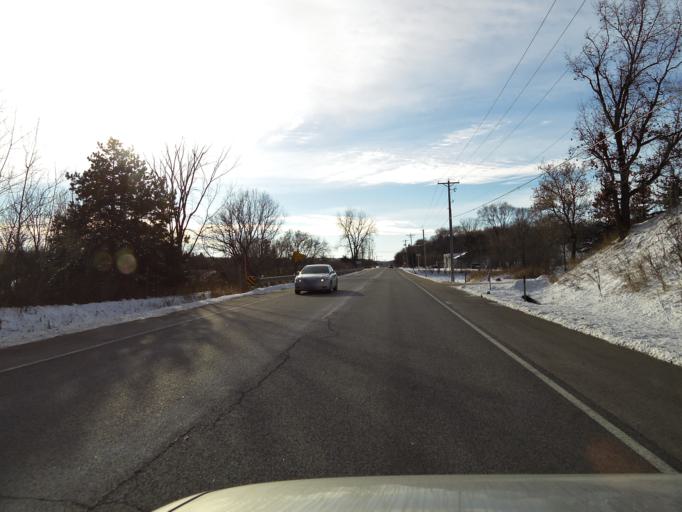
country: US
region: Minnesota
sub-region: Dakota County
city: Inver Grove Heights
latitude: 44.8510
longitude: -93.0854
